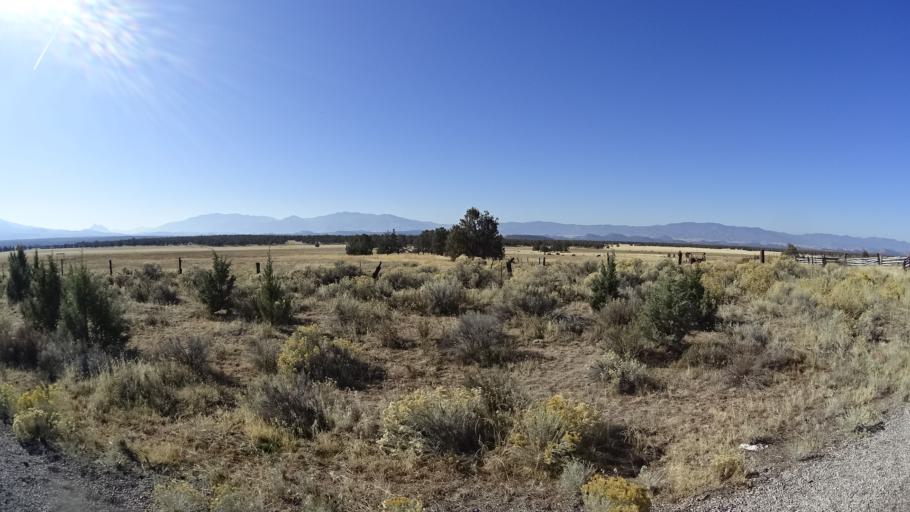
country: US
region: California
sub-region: Siskiyou County
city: Weed
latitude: 41.6213
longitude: -122.3239
